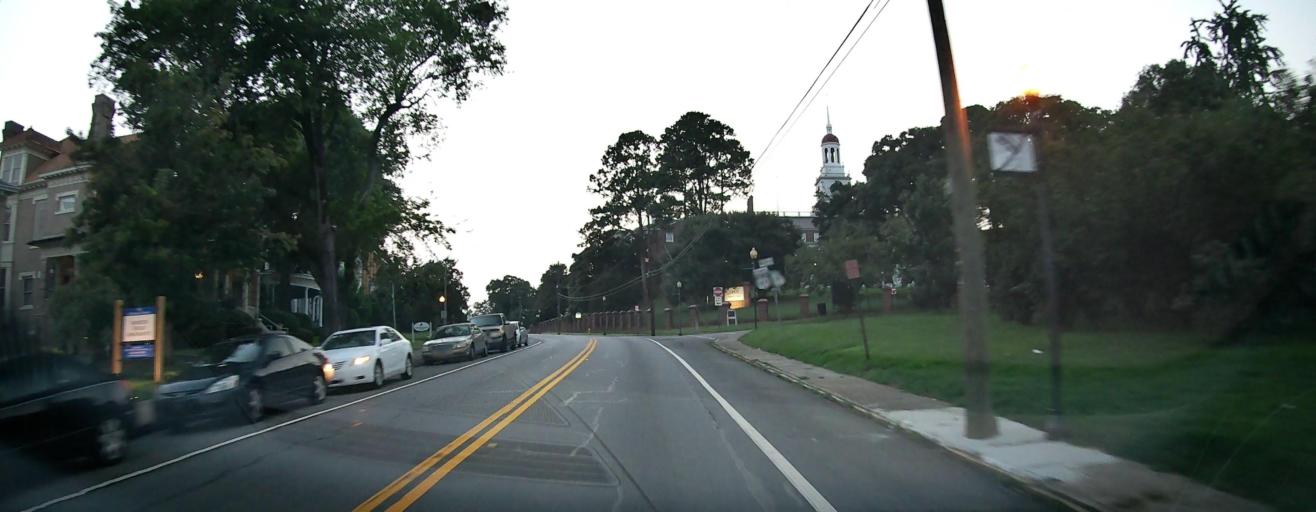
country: US
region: Georgia
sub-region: Bibb County
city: Macon
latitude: 32.8408
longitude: -83.6336
